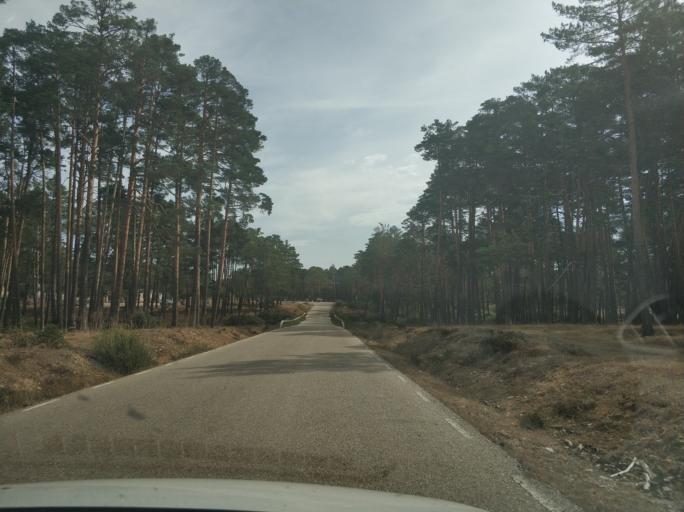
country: ES
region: Castille and Leon
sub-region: Provincia de Soria
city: Navaleno
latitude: 41.8557
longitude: -2.9492
